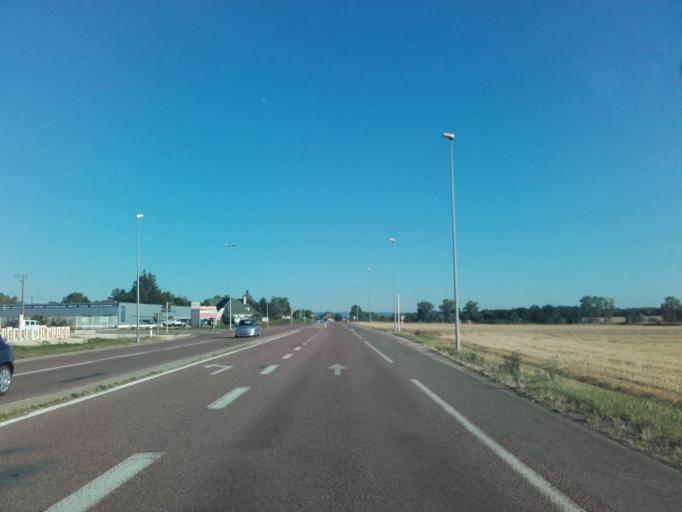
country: FR
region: Bourgogne
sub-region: Departement de Saone-et-Loire
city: Champforgeuil
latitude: 46.8415
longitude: 4.8146
